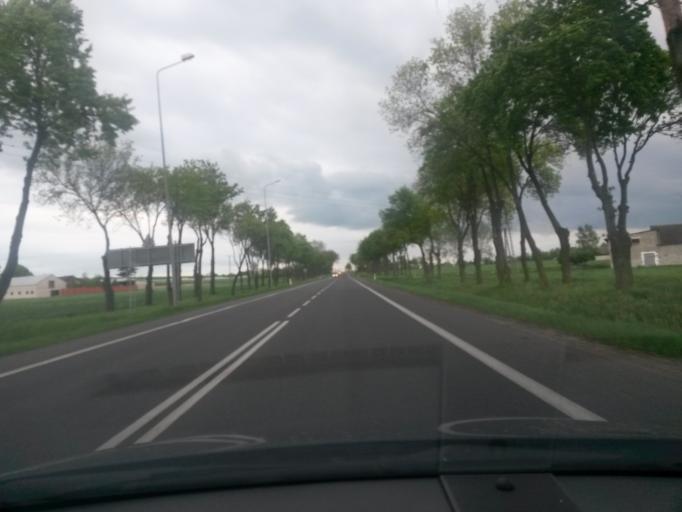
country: PL
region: Masovian Voivodeship
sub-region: Powiat plonski
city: Plonsk
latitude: 52.6042
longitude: 20.3965
